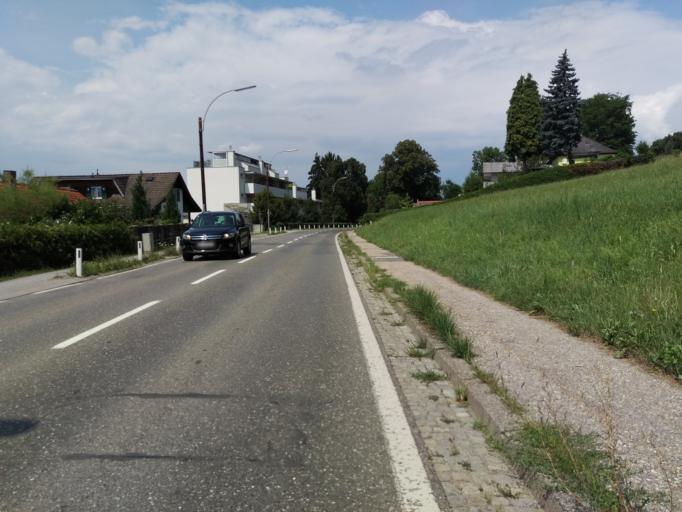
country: AT
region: Styria
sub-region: Politischer Bezirk Graz-Umgebung
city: Raaba
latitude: 47.0368
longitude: 15.4913
